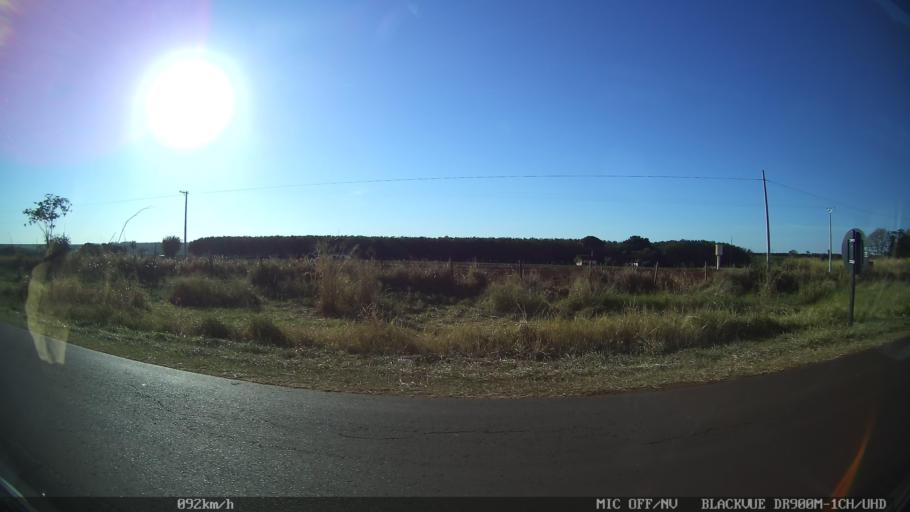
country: BR
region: Sao Paulo
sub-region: Guapiacu
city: Guapiacu
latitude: -20.7512
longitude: -49.1381
